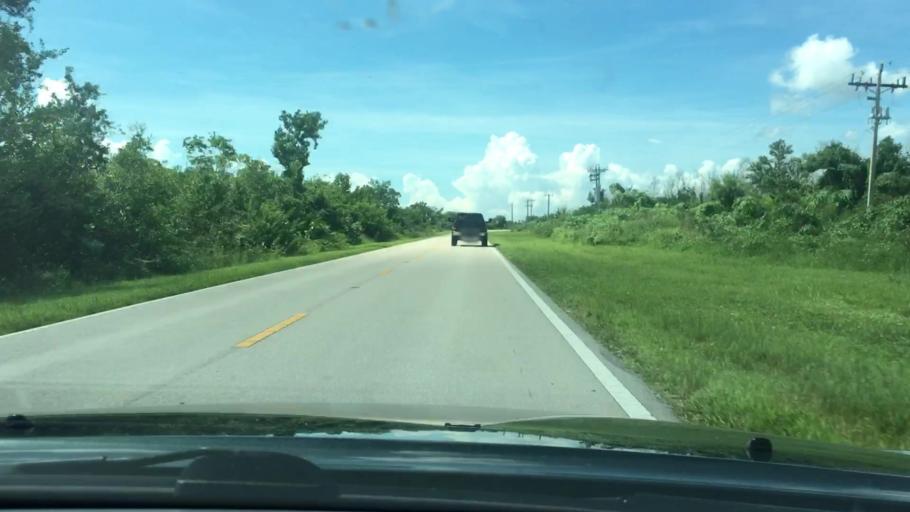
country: US
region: Florida
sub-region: Collier County
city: Marco
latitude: 25.9379
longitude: -81.6471
